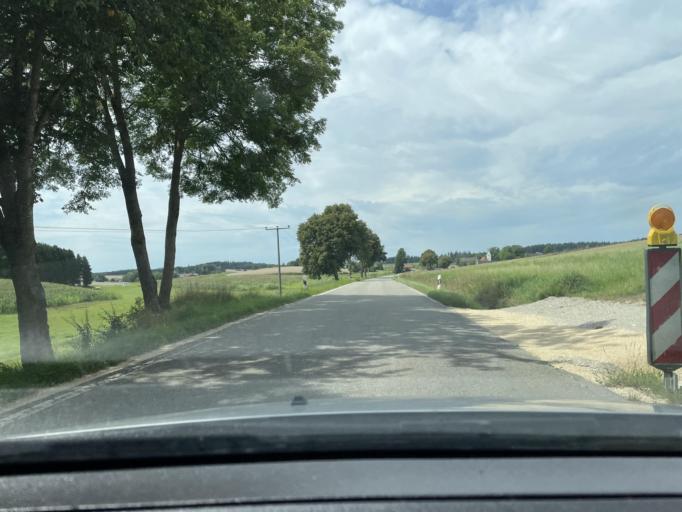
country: DE
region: Bavaria
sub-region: Lower Bavaria
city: Geisenhausen
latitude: 48.4412
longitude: 12.2646
